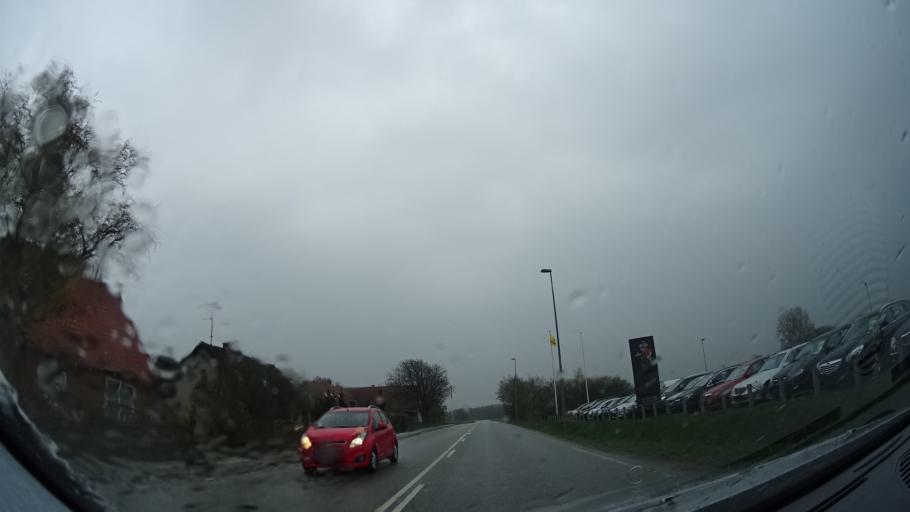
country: DK
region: Zealand
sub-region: Odsherred Kommune
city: Hojby
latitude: 55.8478
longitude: 11.5738
